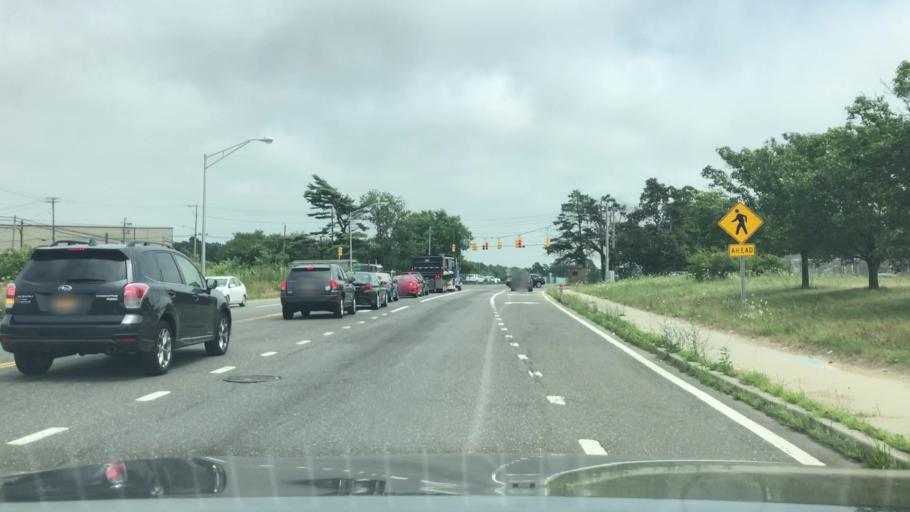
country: US
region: New York
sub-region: Suffolk County
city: East Farmingdale
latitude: 40.7412
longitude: -73.4146
